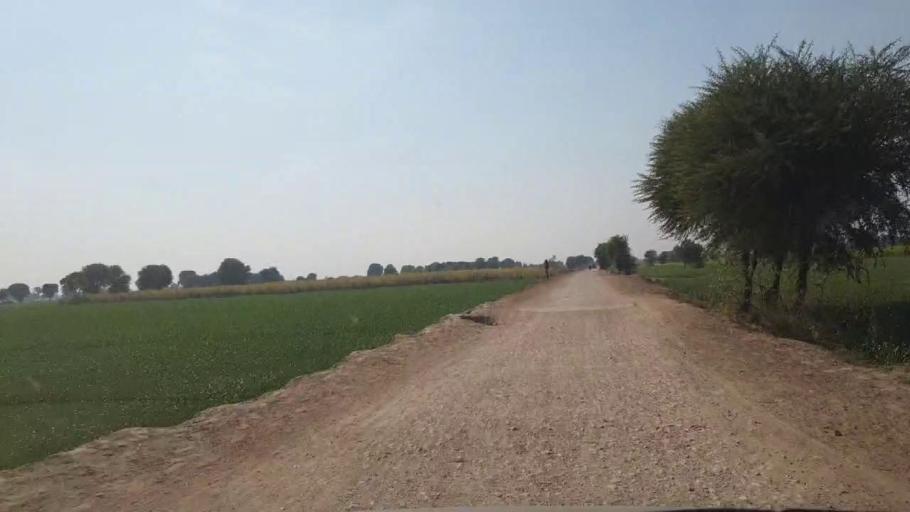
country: PK
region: Sindh
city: Chambar
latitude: 25.3444
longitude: 68.8183
